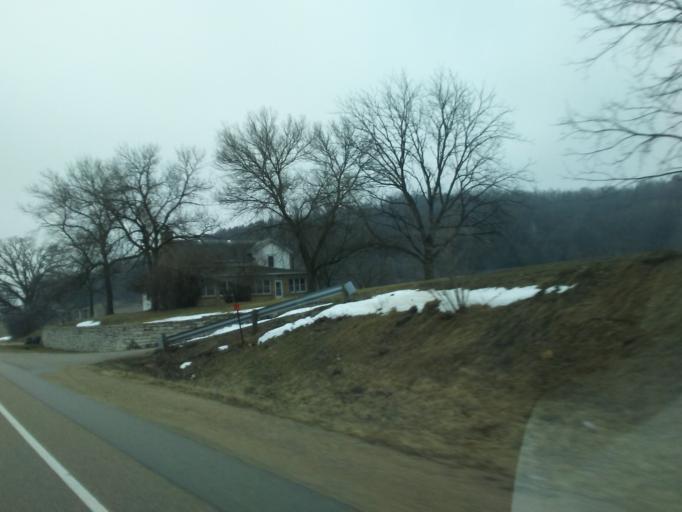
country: US
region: Wisconsin
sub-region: Dane County
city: Black Earth
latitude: 43.1461
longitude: -89.7571
